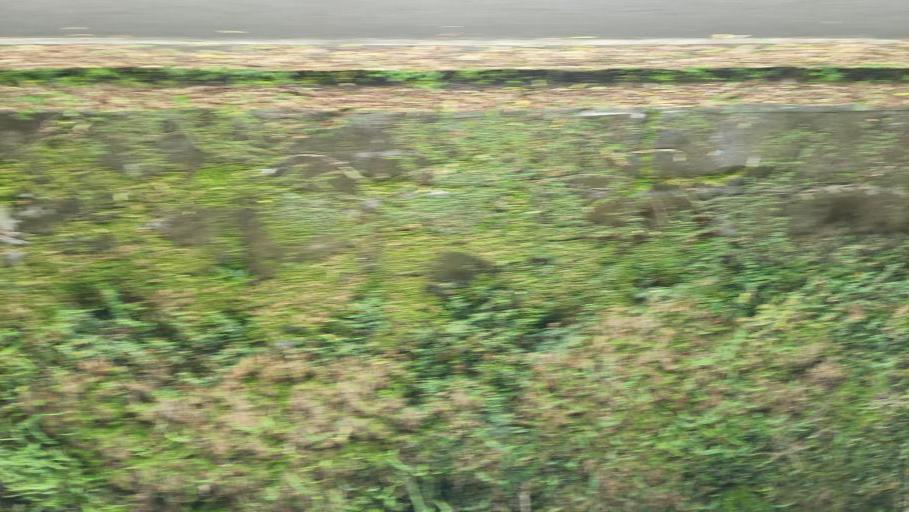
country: TW
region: Taiwan
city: Daxi
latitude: 24.8427
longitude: 121.4496
